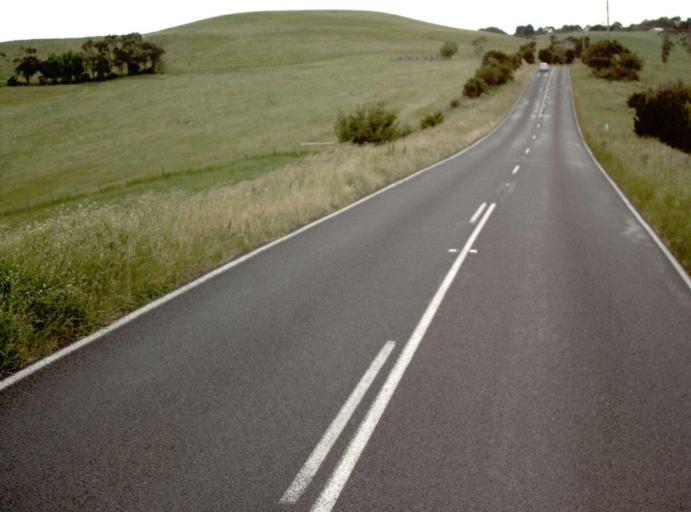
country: AU
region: Victoria
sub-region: Bass Coast
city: North Wonthaggi
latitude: -38.4577
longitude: 145.7919
